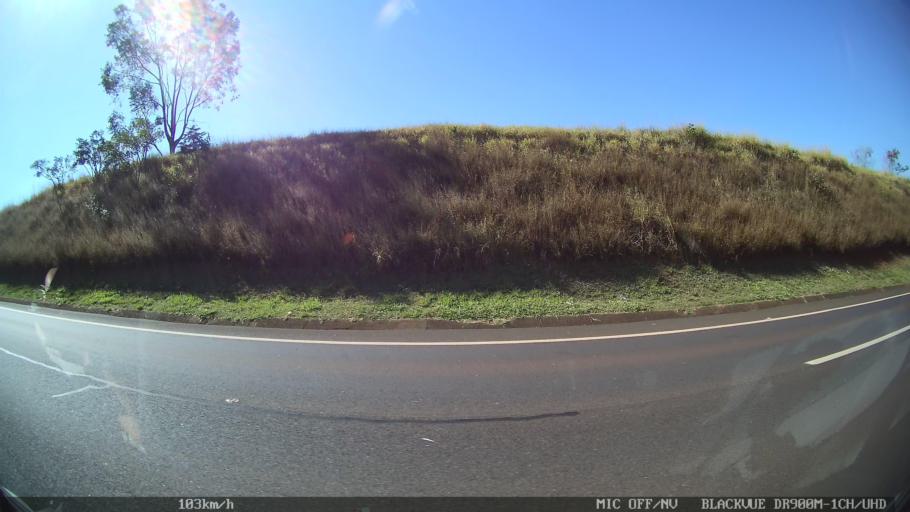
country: BR
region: Sao Paulo
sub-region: Batatais
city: Batatais
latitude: -20.8404
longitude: -47.6015
